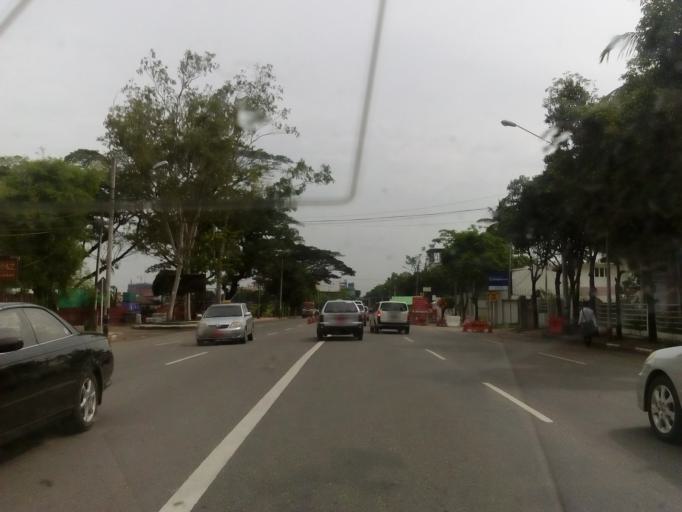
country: MM
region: Yangon
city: Yangon
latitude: 16.8308
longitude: 96.1548
